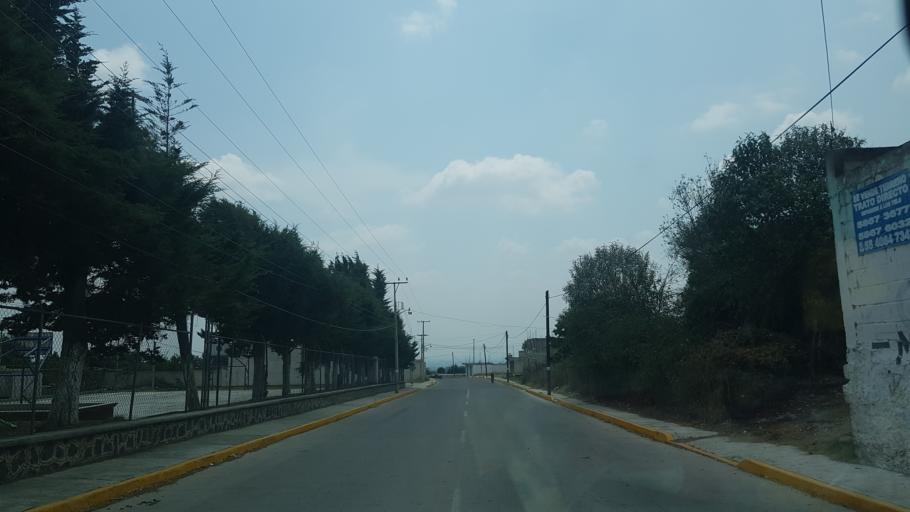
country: MX
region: Puebla
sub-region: Huejotzingo
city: San Juan Pancoac
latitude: 19.1388
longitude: -98.4444
